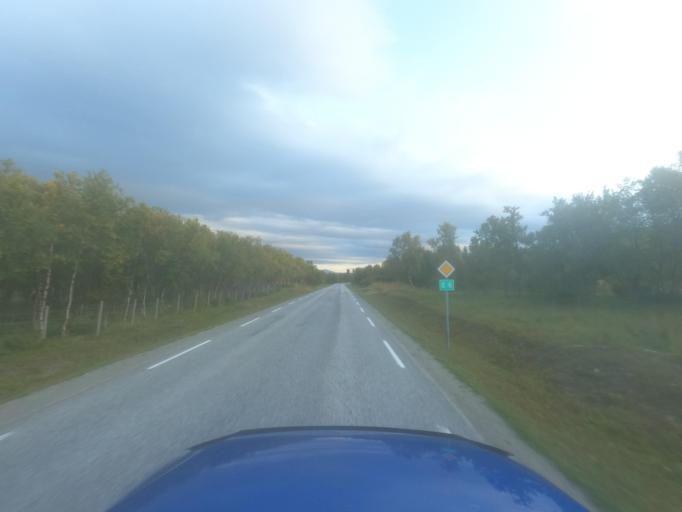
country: NO
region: Finnmark Fylke
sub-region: Porsanger
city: Lakselv
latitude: 70.2774
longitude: 25.0633
